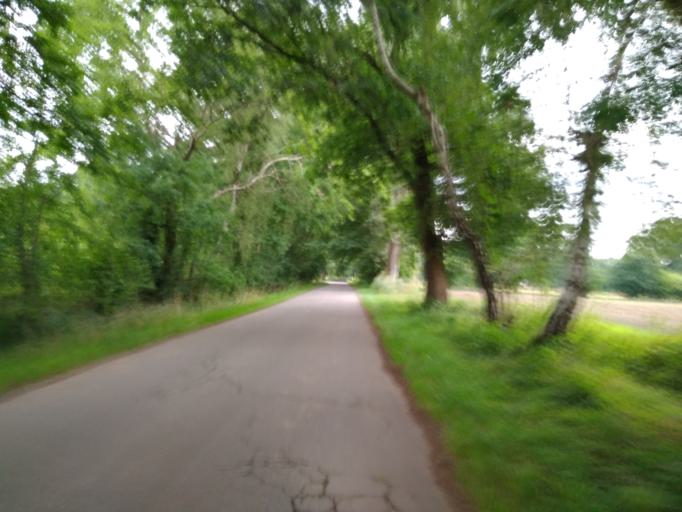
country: DE
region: North Rhine-Westphalia
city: Dorsten
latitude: 51.6279
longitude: 6.9621
